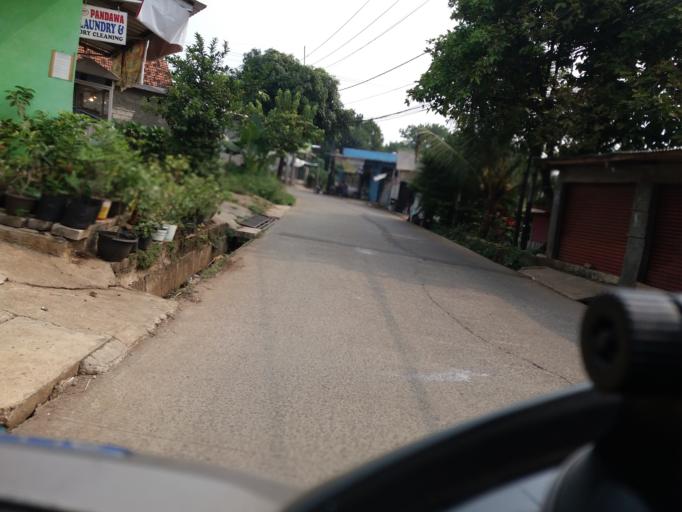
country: ID
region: West Java
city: Cibinong
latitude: -6.4384
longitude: 106.8643
